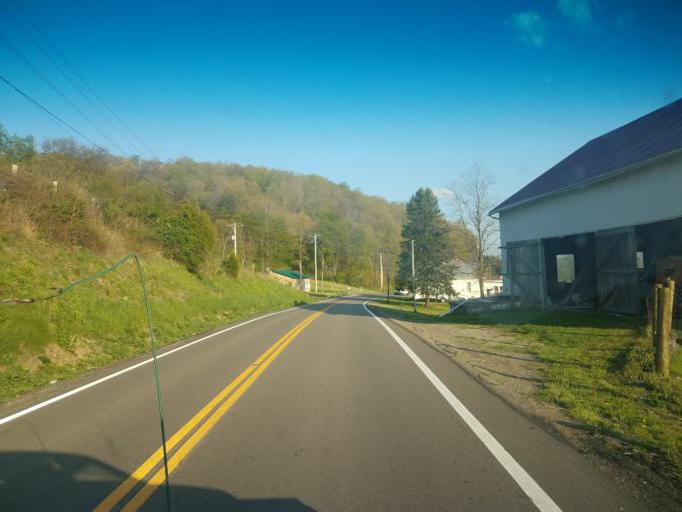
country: US
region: Ohio
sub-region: Holmes County
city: Millersburg
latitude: 40.5185
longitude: -81.9959
